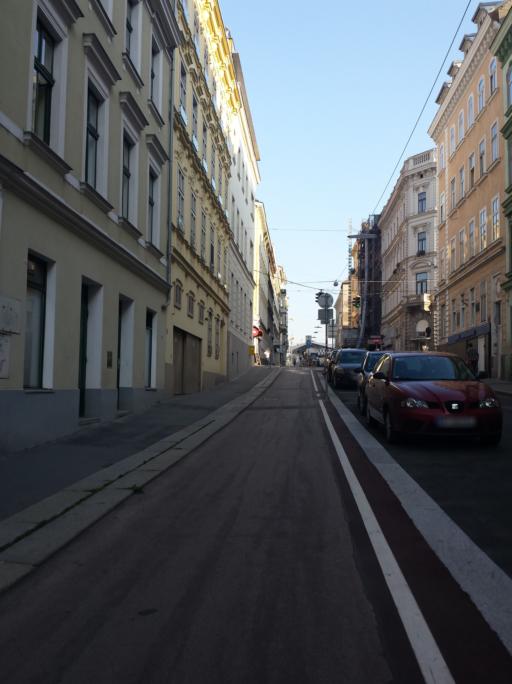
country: AT
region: Vienna
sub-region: Wien Stadt
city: Vienna
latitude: 48.1890
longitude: 16.3764
